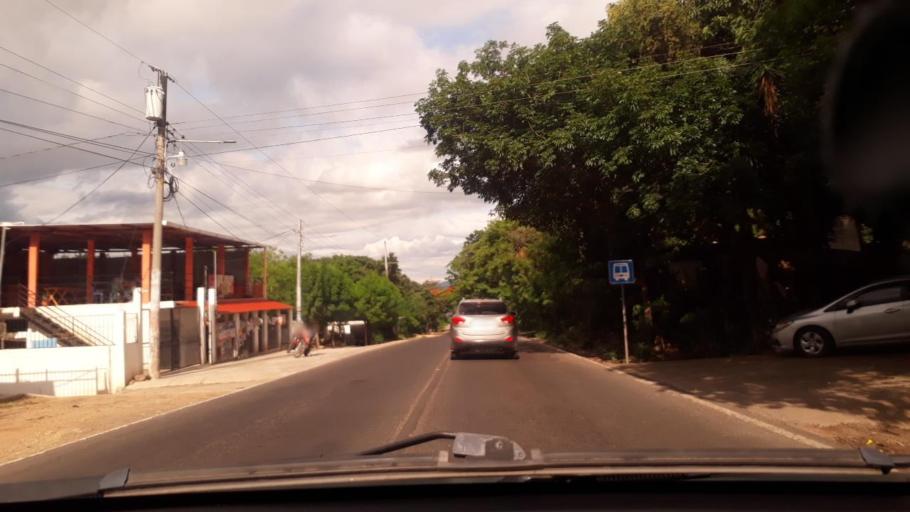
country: GT
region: Jutiapa
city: Quesada
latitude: 14.2769
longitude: -89.9825
